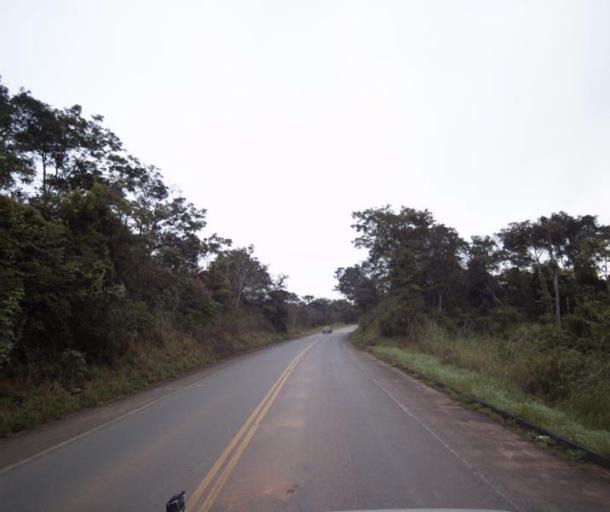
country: BR
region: Goias
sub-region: Pirenopolis
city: Pirenopolis
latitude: -15.8645
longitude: -48.7730
